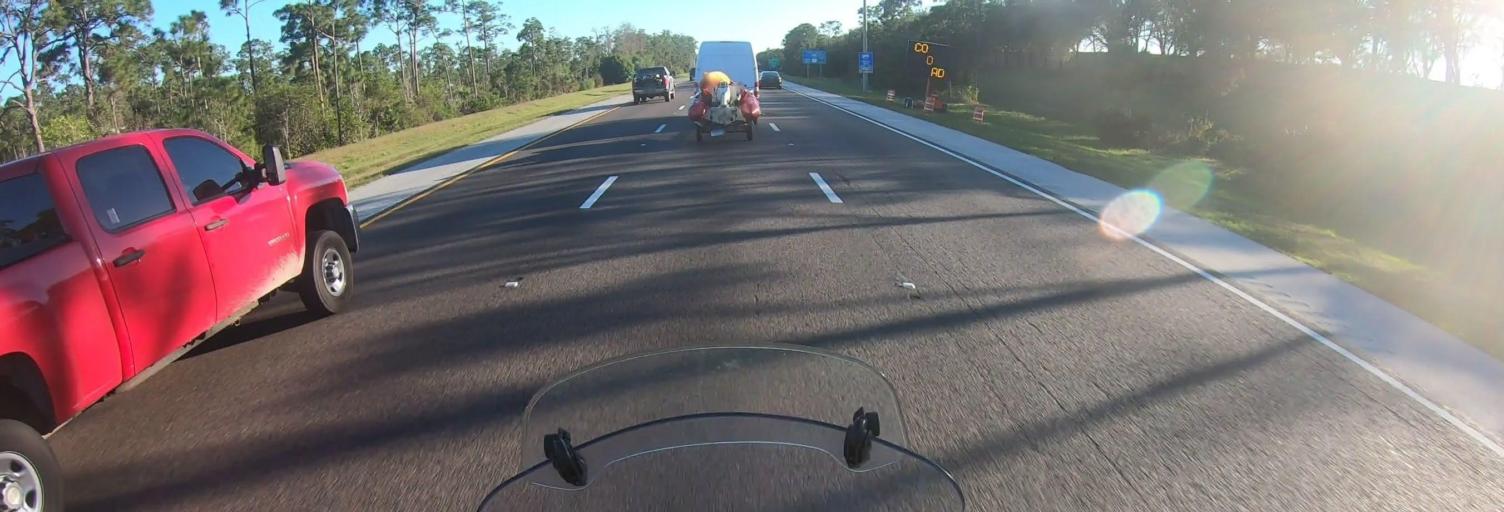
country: US
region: Florida
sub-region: Lee County
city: Gateway
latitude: 26.5644
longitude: -81.7947
